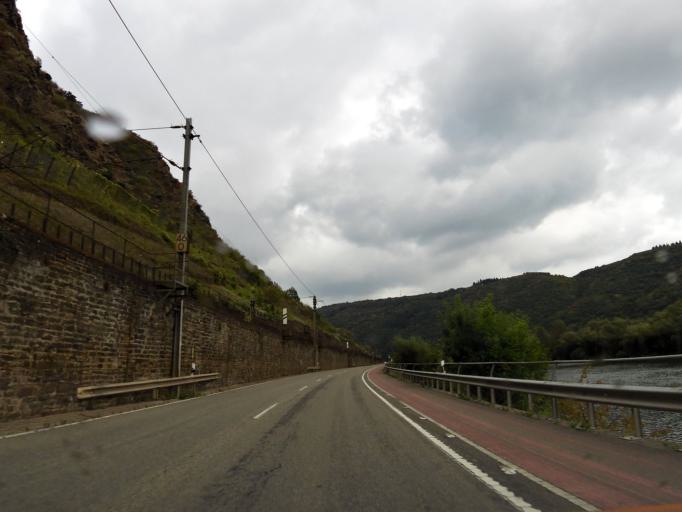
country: DE
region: Rheinland-Pfalz
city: Klotten
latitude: 50.1624
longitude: 7.1824
